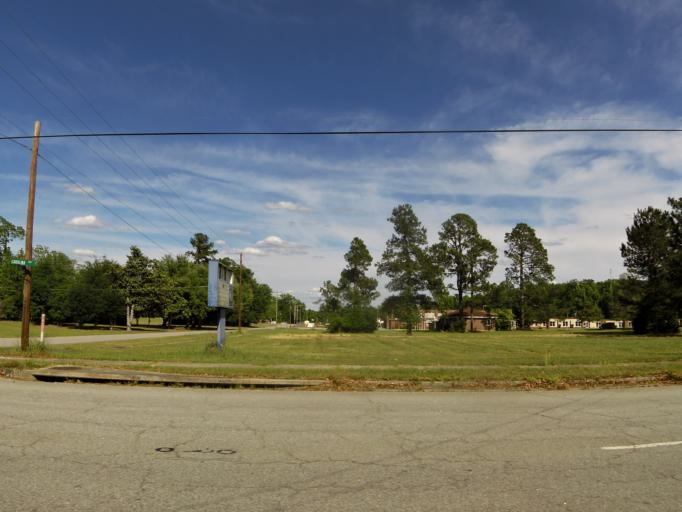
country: US
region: South Carolina
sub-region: Bamberg County
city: Denmark
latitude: 33.3028
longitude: -81.1452
